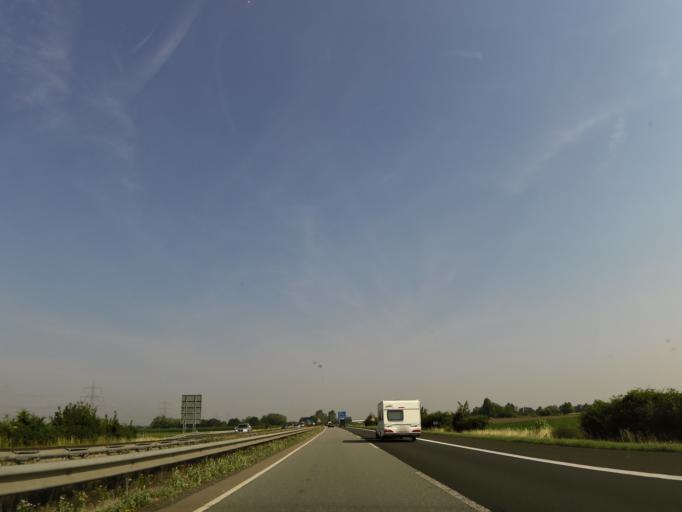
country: DE
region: Rheinland-Pfalz
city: Mutterstadt
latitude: 49.4219
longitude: 8.3381
